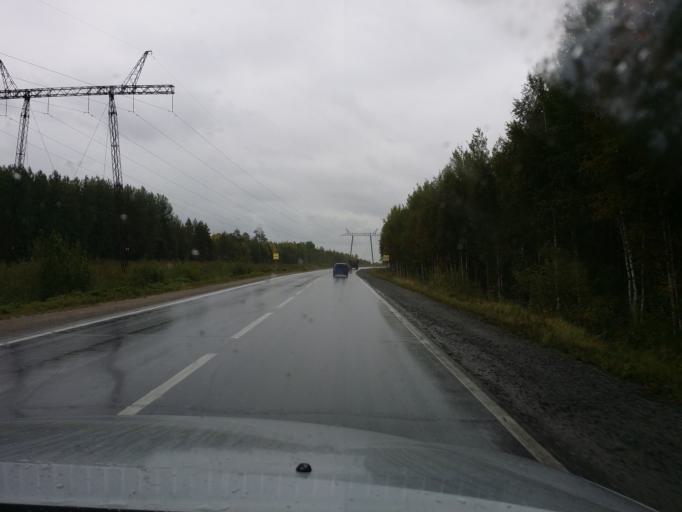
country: RU
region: Khanty-Mansiyskiy Avtonomnyy Okrug
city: Megion
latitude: 61.1605
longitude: 75.7206
